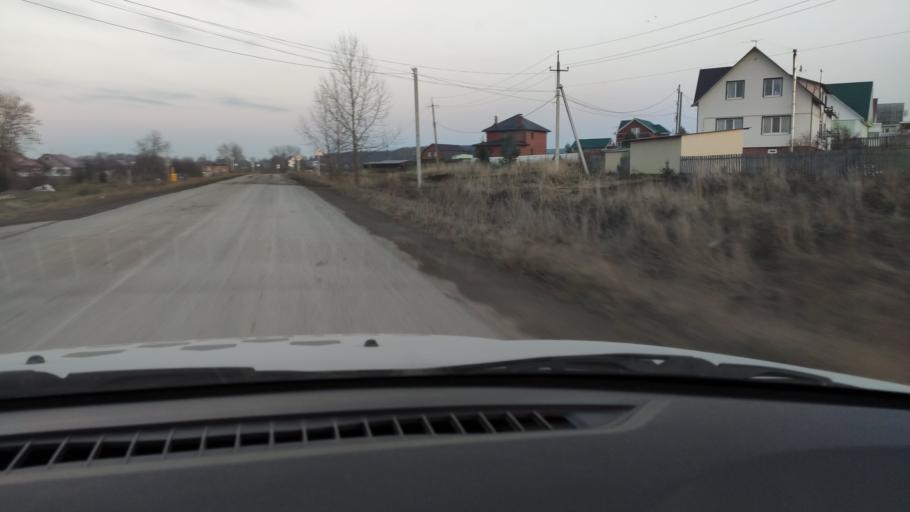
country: RU
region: Perm
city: Lobanovo
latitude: 57.8072
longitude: 56.3586
